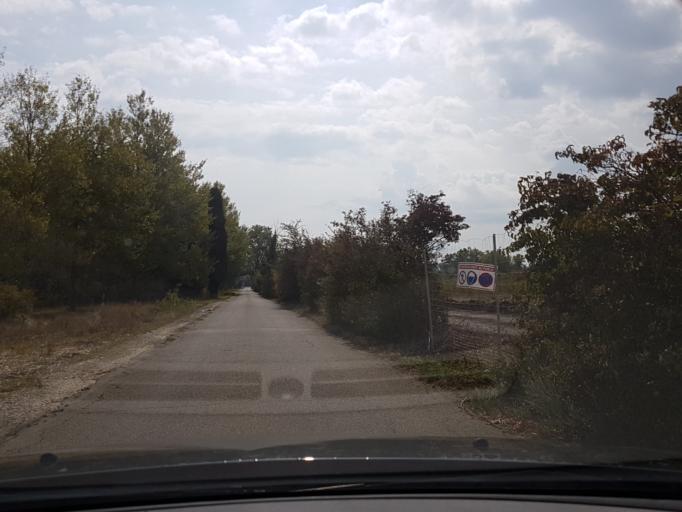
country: FR
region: Provence-Alpes-Cote d'Azur
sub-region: Departement du Vaucluse
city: Saint-Saturnin-les-Avignon
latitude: 43.9777
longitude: 4.9396
